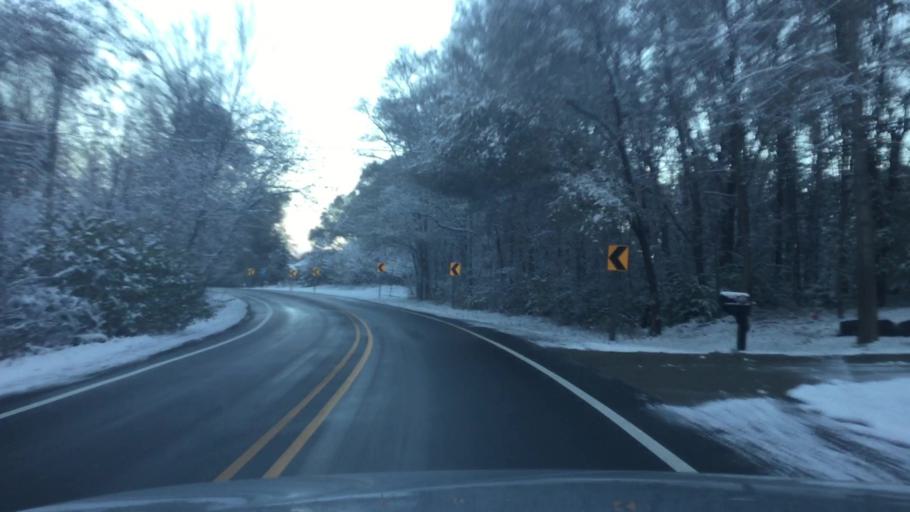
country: US
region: Michigan
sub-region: Oakland County
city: West Bloomfield Township
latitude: 42.5918
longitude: -83.4255
